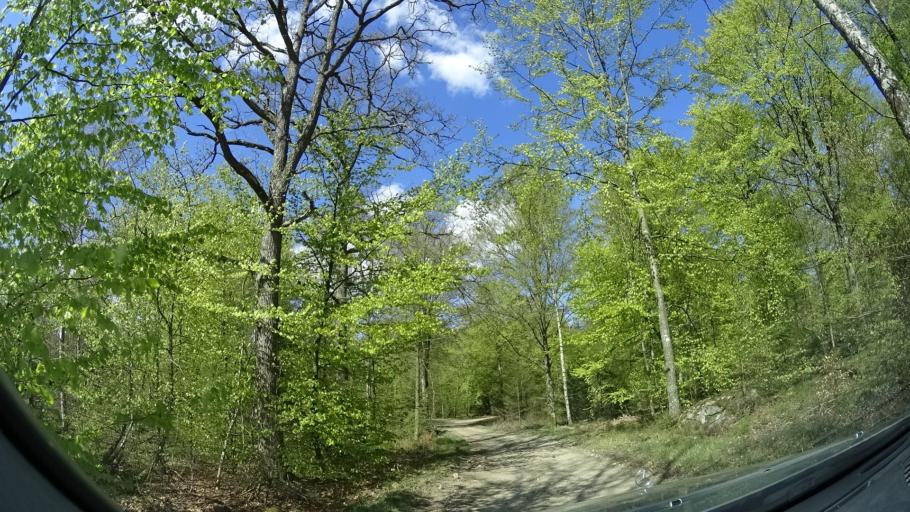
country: SE
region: Skane
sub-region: Hassleholms Kommun
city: Tormestorp
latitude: 56.0925
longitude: 13.6918
